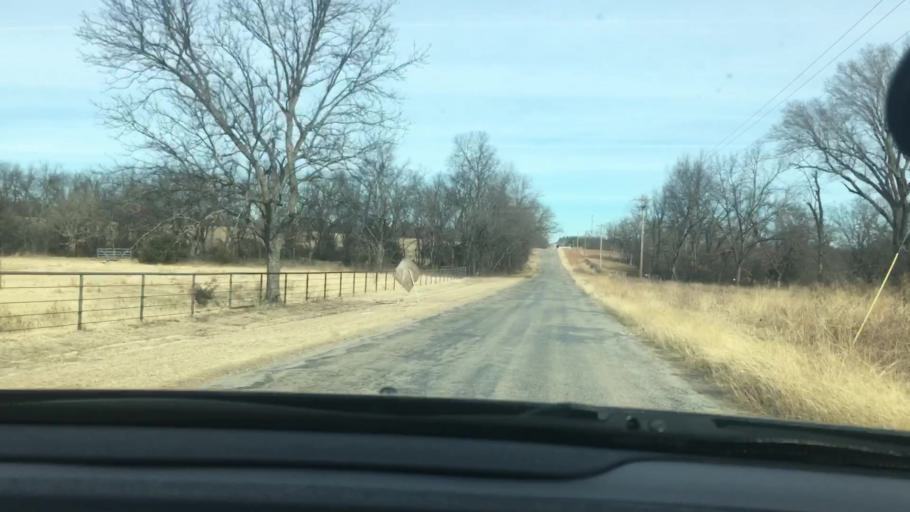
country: US
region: Oklahoma
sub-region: Garvin County
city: Wynnewood
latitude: 34.6402
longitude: -97.2475
